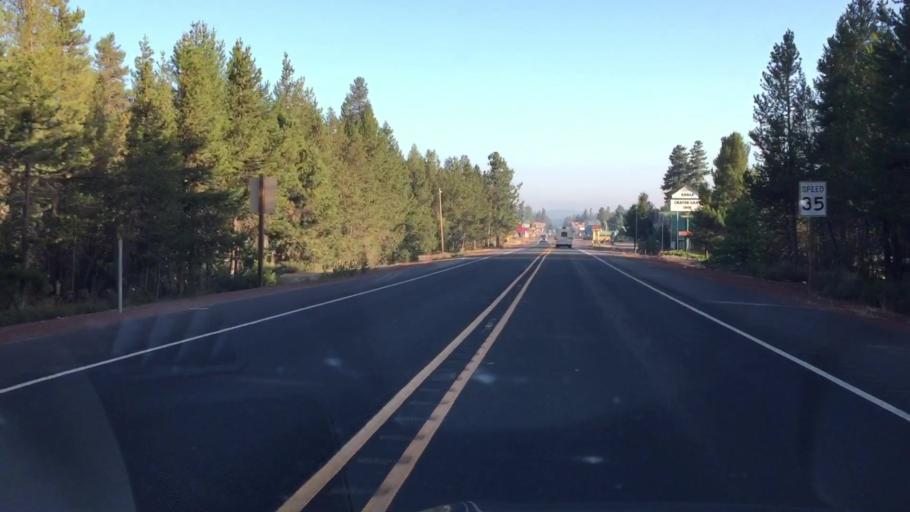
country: US
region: Oregon
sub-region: Deschutes County
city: La Pine
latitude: 43.2106
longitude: -121.7804
